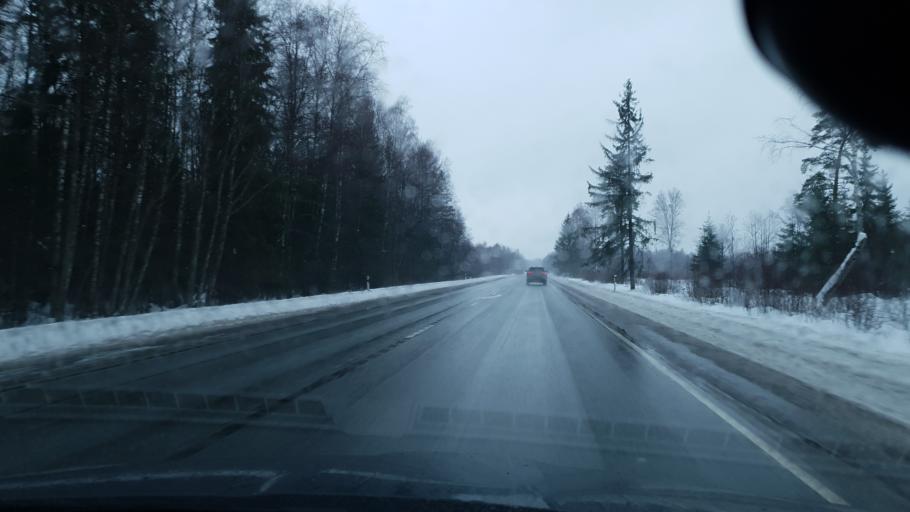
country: EE
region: Harju
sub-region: Anija vald
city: Kehra
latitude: 59.1549
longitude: 25.2926
